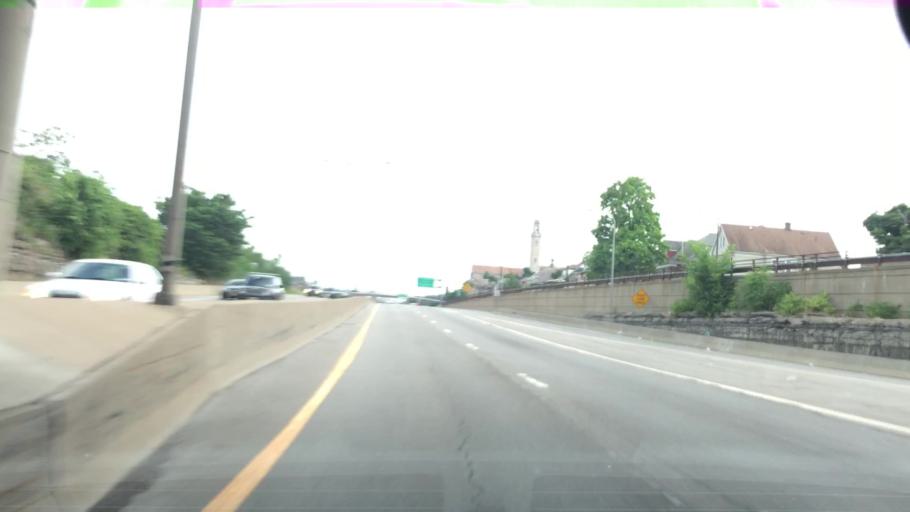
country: US
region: New York
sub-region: Erie County
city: Buffalo
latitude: 42.9219
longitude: -78.8435
